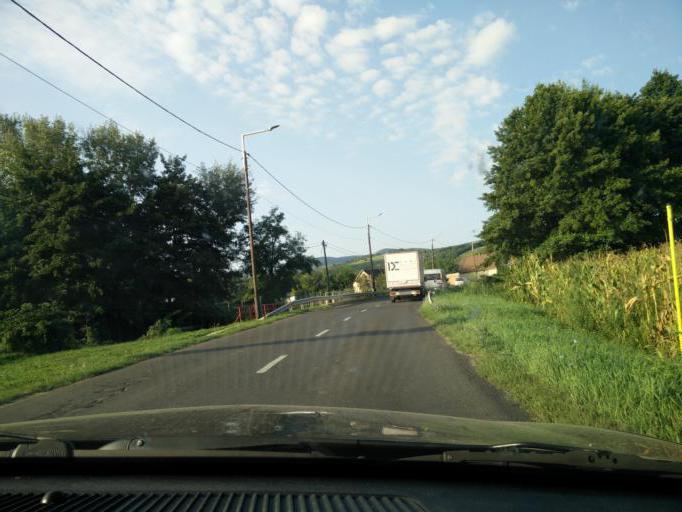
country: HU
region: Baranya
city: Szaszvar
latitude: 46.2760
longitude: 18.4021
